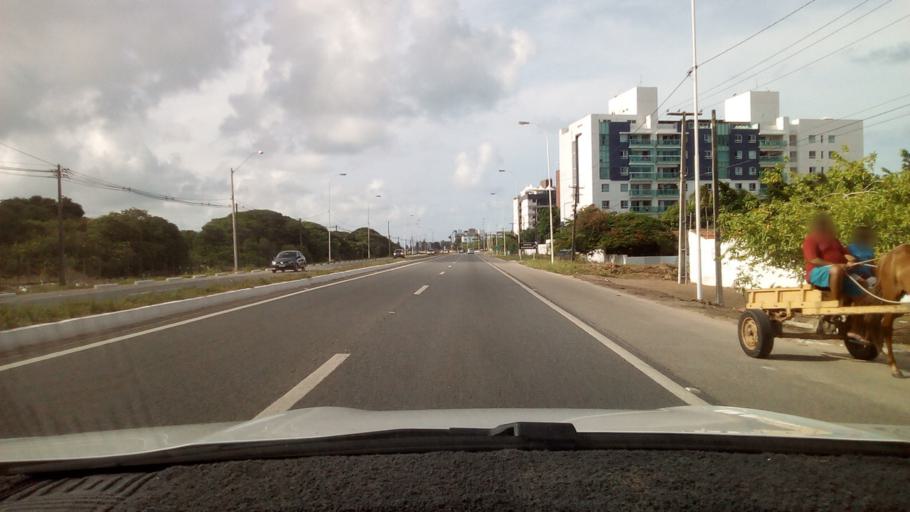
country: BR
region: Paraiba
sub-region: Cabedelo
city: Cabedelo
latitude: -6.9988
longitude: -34.8283
